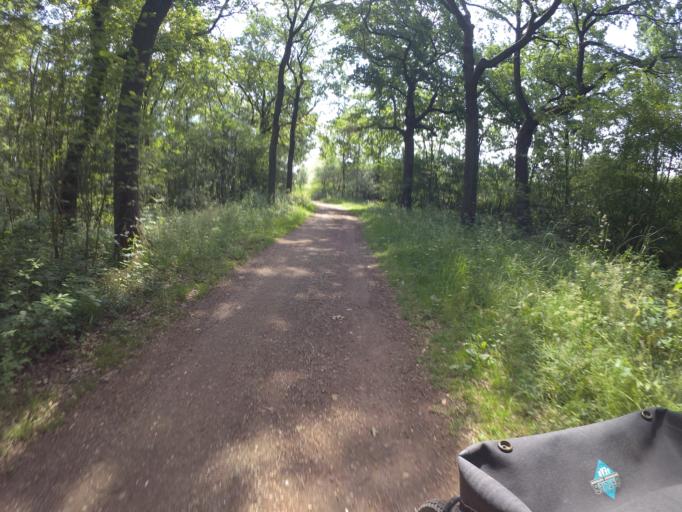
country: NL
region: North Brabant
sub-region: Gemeente Haaren
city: Haaren
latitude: 51.5872
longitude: 5.2401
